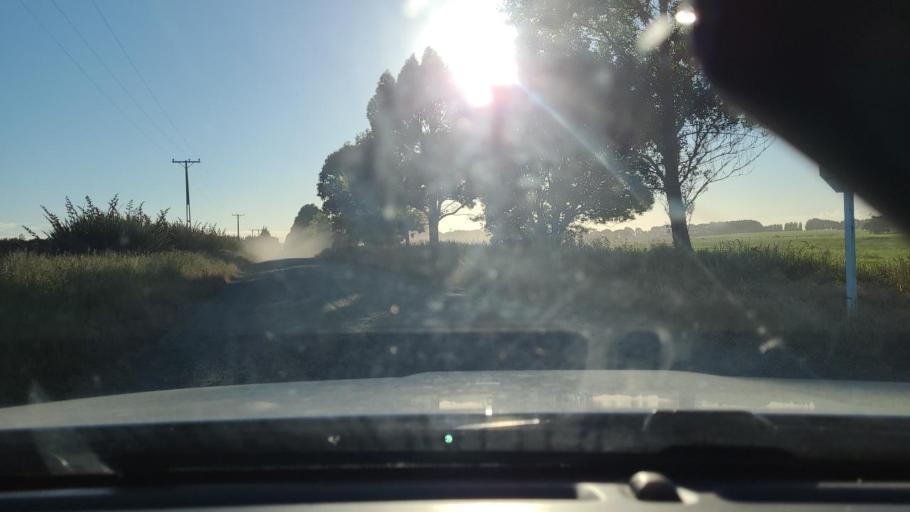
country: NZ
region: Southland
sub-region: Southland District
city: Winton
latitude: -46.2268
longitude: 168.3188
